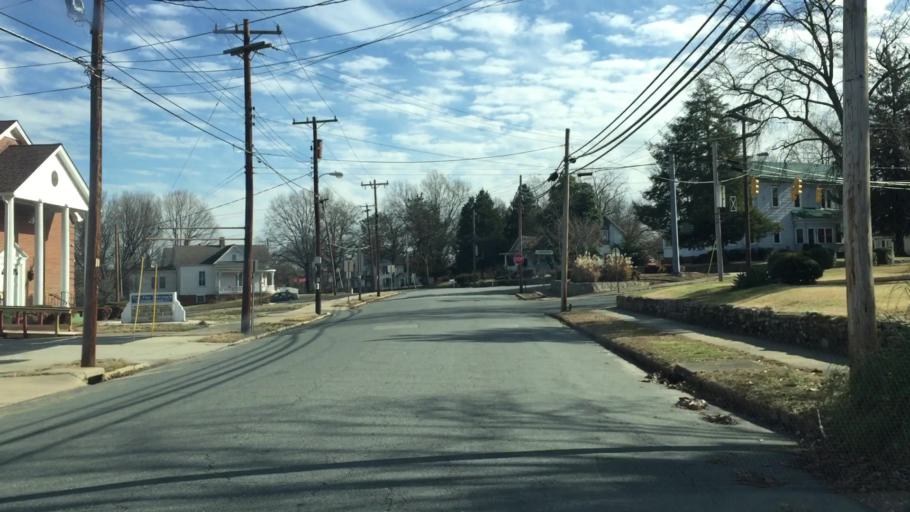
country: US
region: North Carolina
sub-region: Rockingham County
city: Reidsville
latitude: 36.3572
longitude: -79.6591
